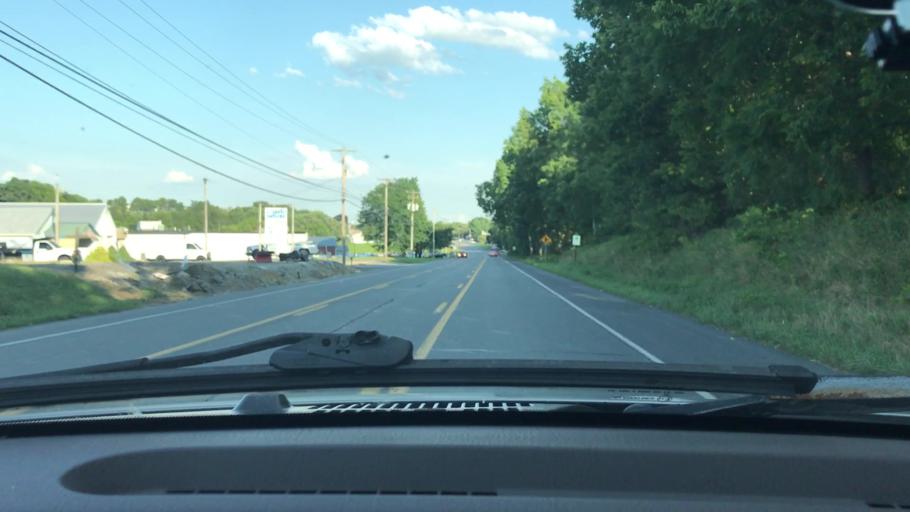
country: US
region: Pennsylvania
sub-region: Lancaster County
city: Rheems
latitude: 40.1211
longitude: -76.5410
